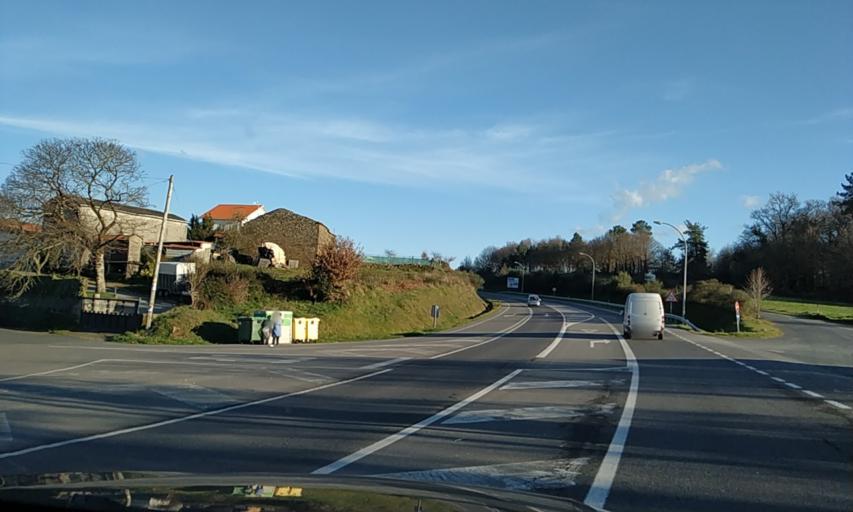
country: ES
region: Galicia
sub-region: Provincia de Pontevedra
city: Lalin
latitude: 42.6753
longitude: -8.1642
